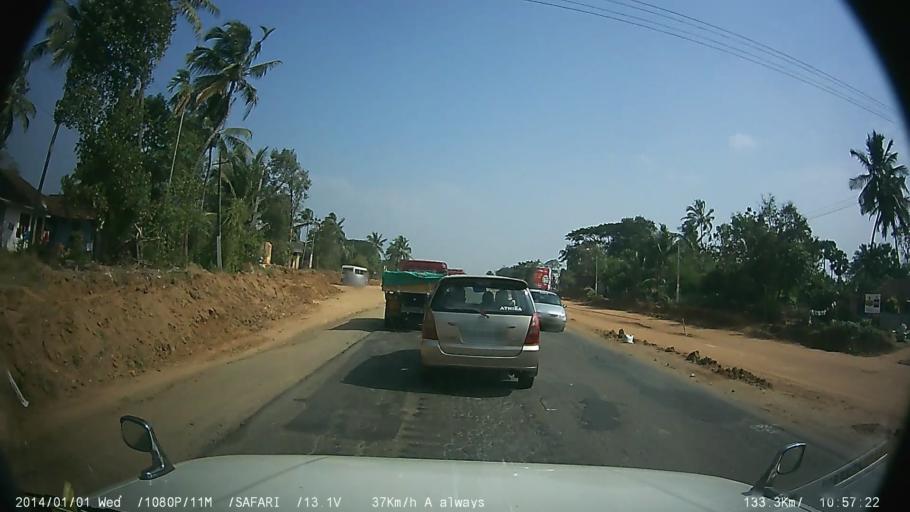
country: IN
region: Kerala
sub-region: Palakkad district
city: Palakkad
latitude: 10.7327
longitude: 76.6123
